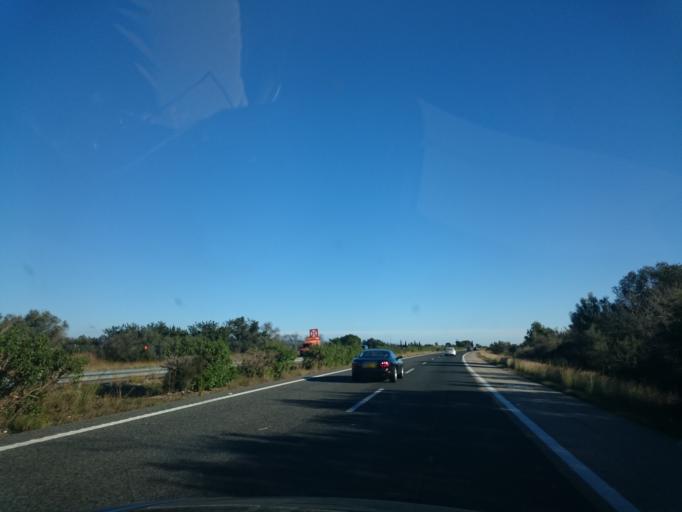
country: ES
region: Catalonia
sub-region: Provincia de Tarragona
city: Masdenverge
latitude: 40.6928
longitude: 0.5323
